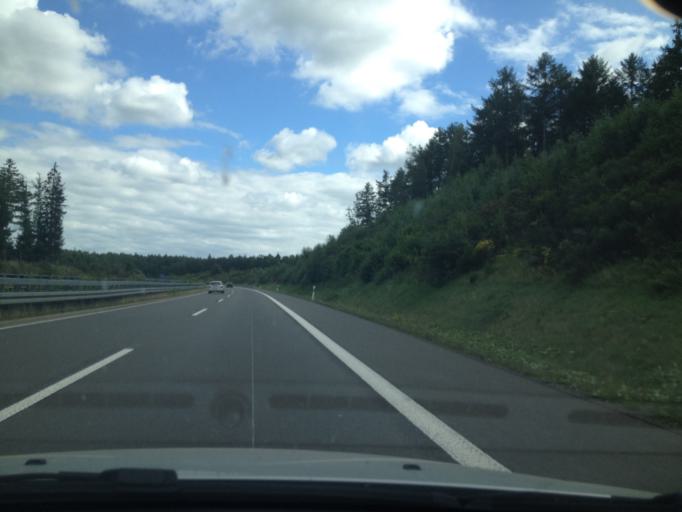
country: DE
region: North Rhine-Westphalia
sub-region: Regierungsbezirk Arnsberg
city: Wenden
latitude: 50.9929
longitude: 7.8996
